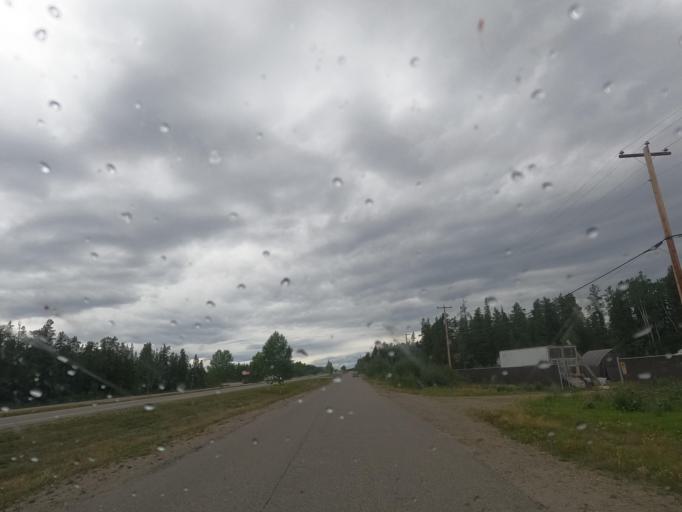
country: CA
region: Yukon
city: Watson Lake
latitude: 60.0520
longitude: -128.6612
